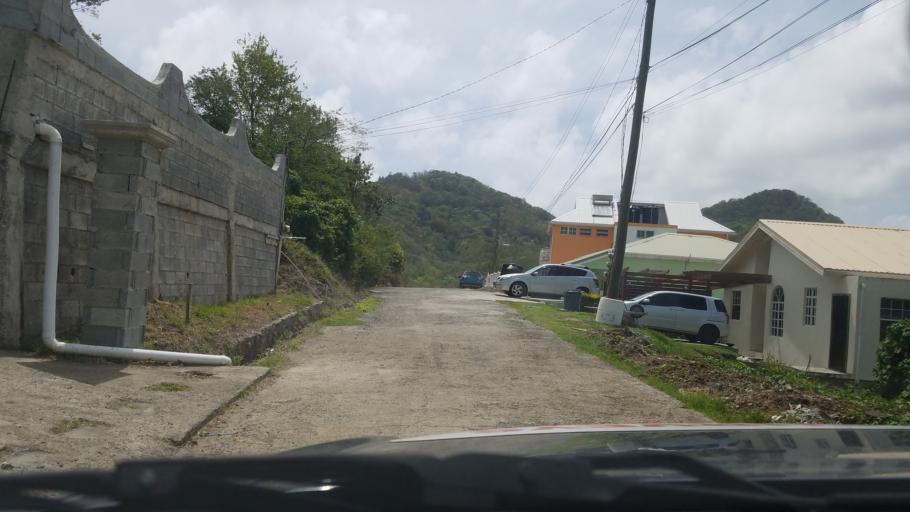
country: LC
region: Gros-Islet
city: Gros Islet
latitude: 14.0474
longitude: -60.9563
